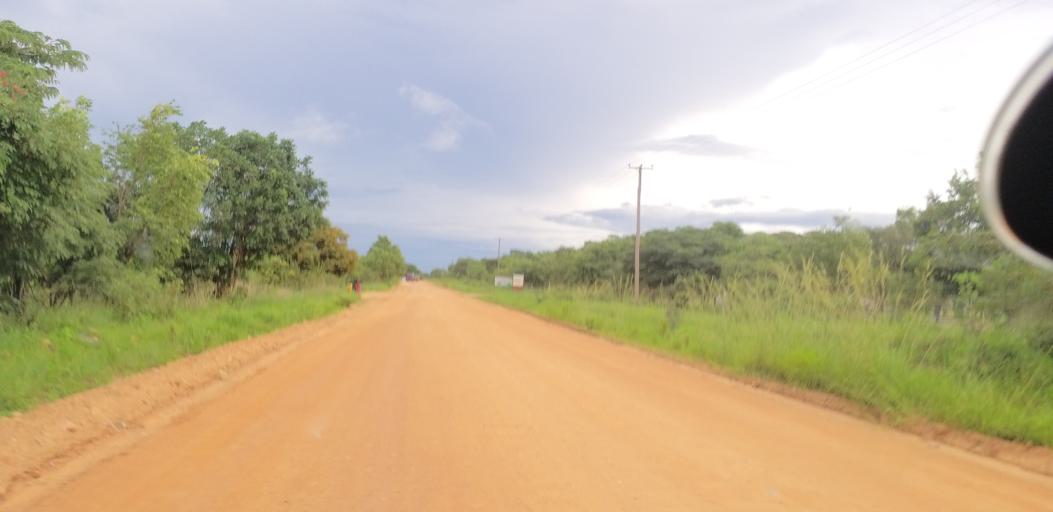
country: ZM
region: Lusaka
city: Chongwe
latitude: -15.1785
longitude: 28.4569
